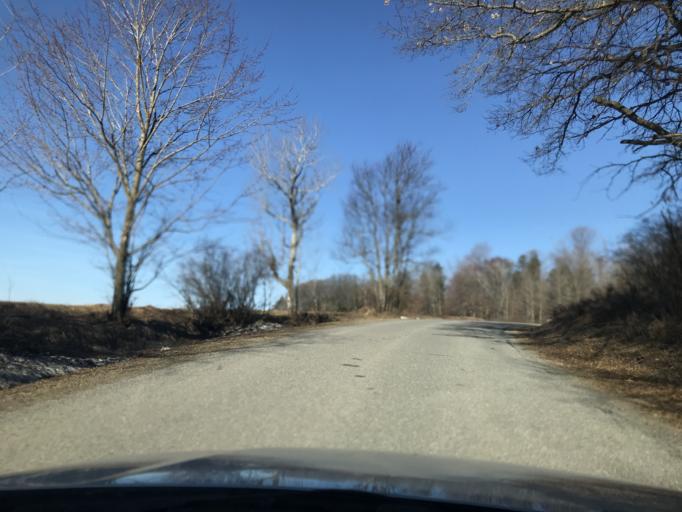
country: US
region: Wisconsin
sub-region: Marinette County
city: Niagara
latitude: 45.3807
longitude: -88.0379
